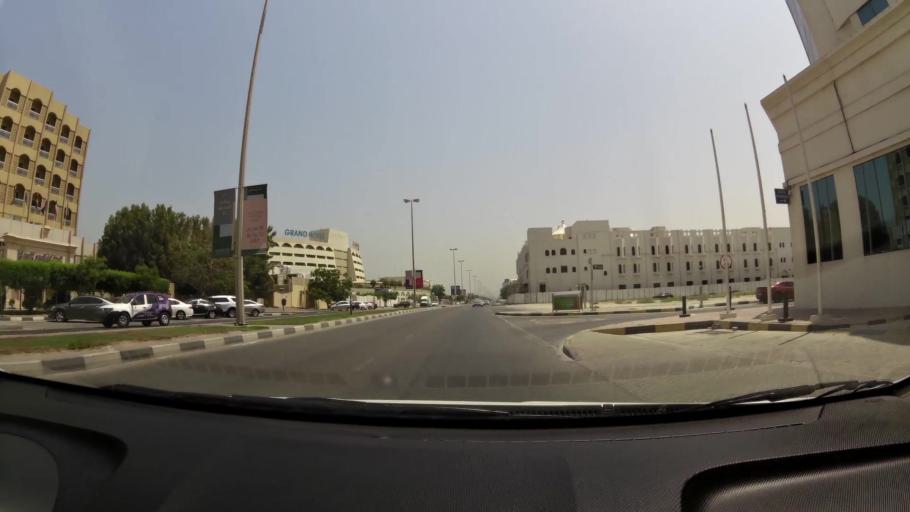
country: AE
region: Ash Shariqah
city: Sharjah
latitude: 25.3370
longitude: 55.3619
